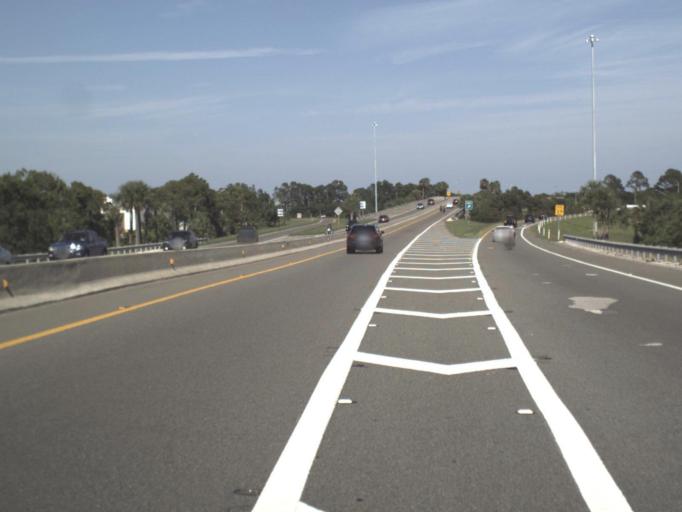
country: US
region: Florida
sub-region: Saint Johns County
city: Ponte Vedra Beach
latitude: 30.2562
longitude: -81.3929
